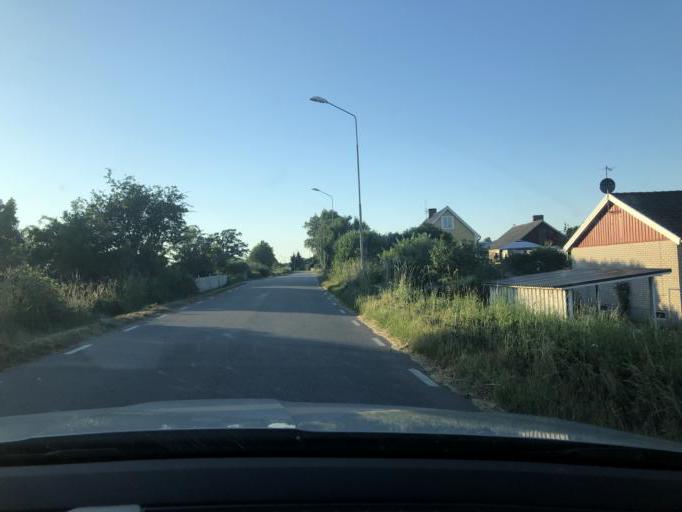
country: SE
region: Blekinge
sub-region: Karlshamns Kommun
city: Morrum
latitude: 56.1218
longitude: 14.6702
